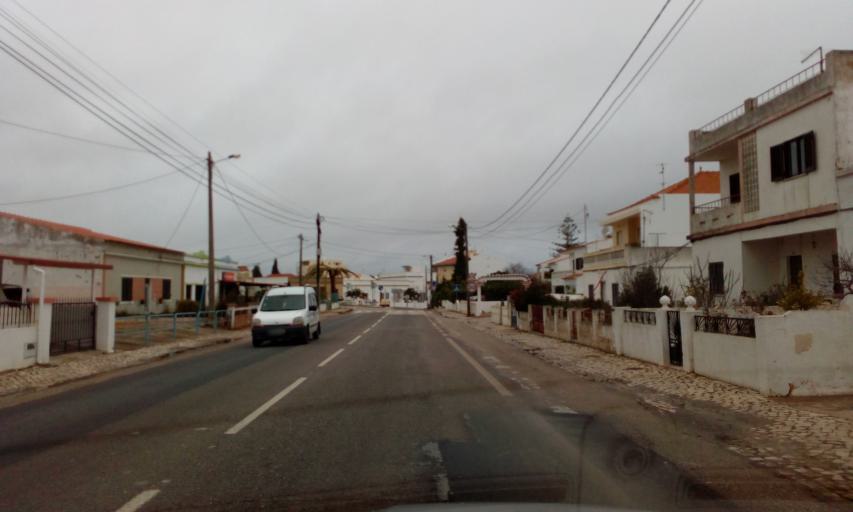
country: PT
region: Faro
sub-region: Albufeira
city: Guia
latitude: 37.1616
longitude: -8.3000
